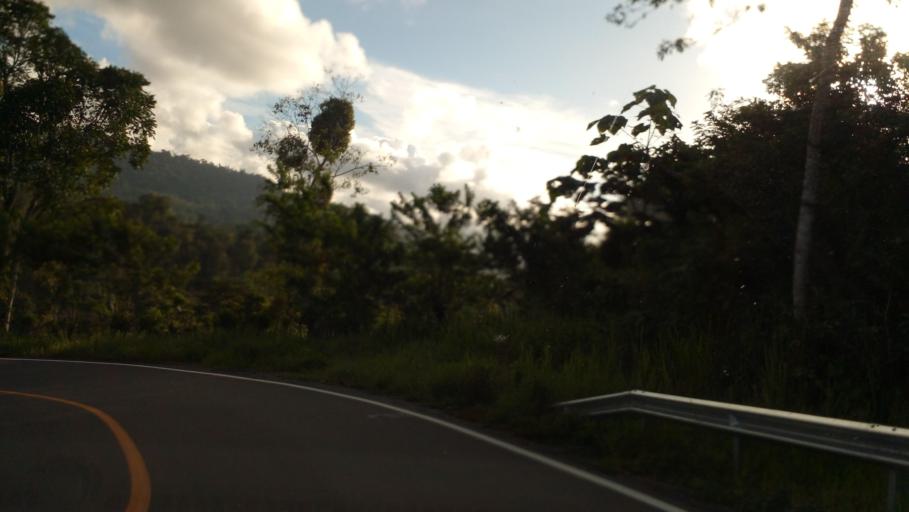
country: PA
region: Bocas del Toro
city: Almirante
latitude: 9.3273
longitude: -82.4620
